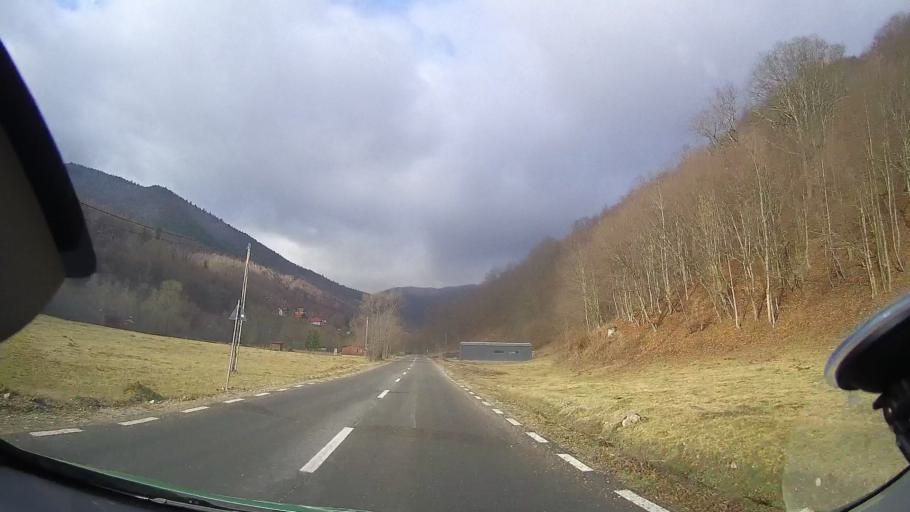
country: RO
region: Cluj
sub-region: Comuna Valea Ierii
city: Valea Ierii
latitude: 46.6389
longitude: 23.3630
